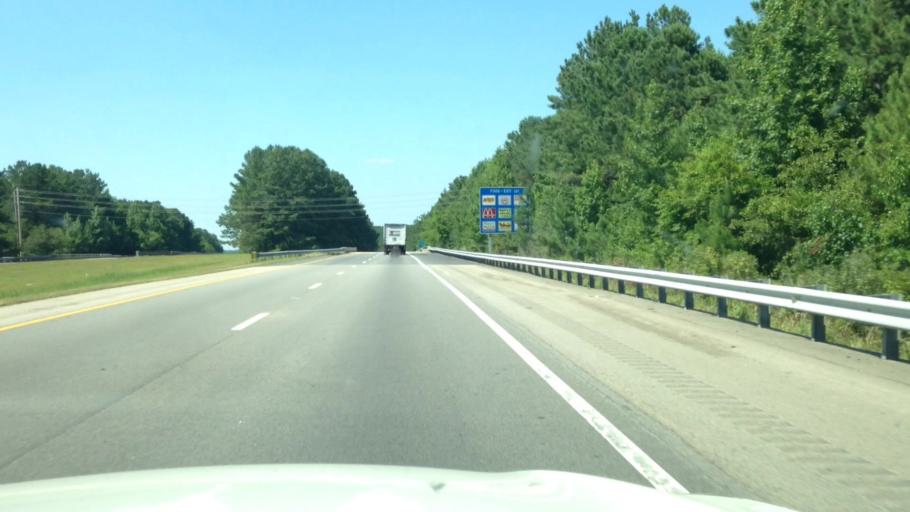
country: US
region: North Carolina
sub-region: Wilson County
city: Wilson
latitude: 35.7463
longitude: -78.0050
